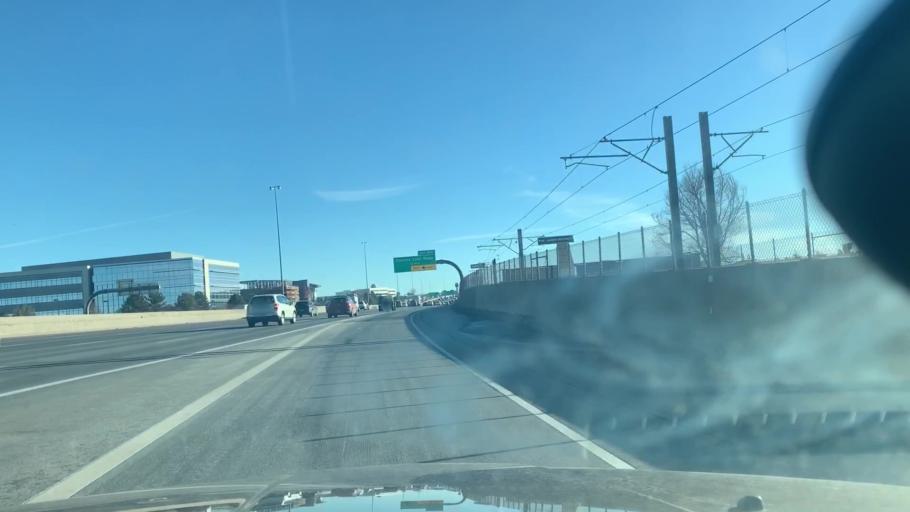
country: US
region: Colorado
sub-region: Arapahoe County
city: Centennial
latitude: 39.5775
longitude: -104.8754
